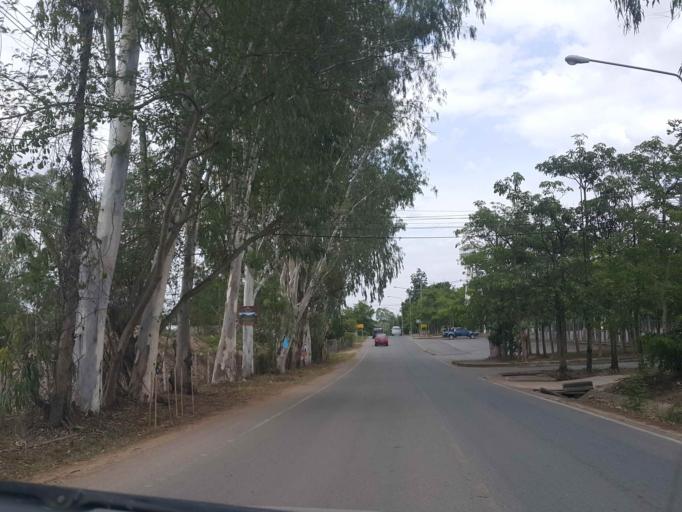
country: TH
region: Chiang Mai
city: Hang Dong
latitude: 18.7551
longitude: 98.9234
